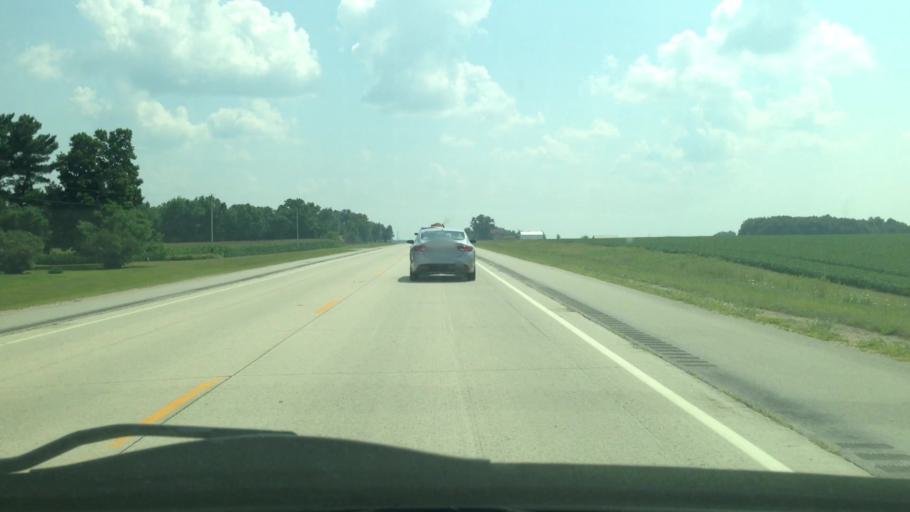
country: US
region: Minnesota
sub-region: Fillmore County
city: Spring Valley
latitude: 43.5213
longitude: -92.3694
